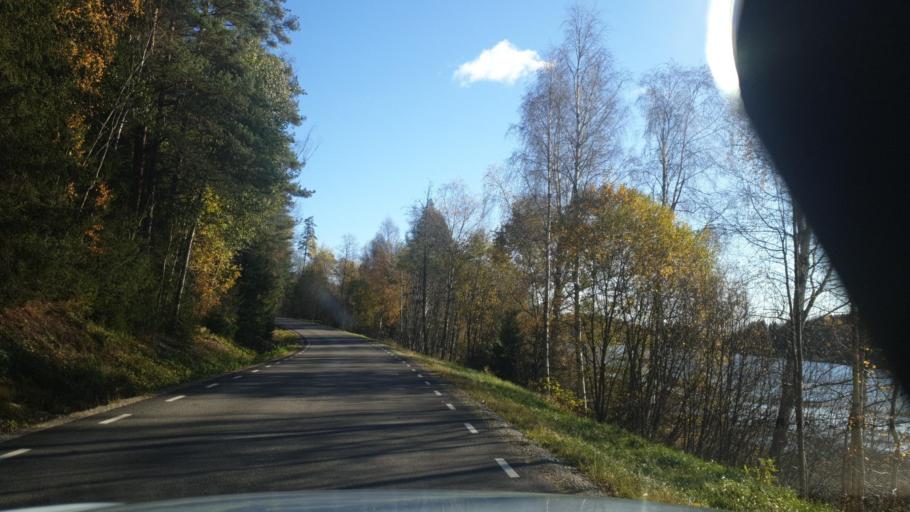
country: SE
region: Vaermland
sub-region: Arvika Kommun
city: Arvika
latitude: 59.6590
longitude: 12.7993
